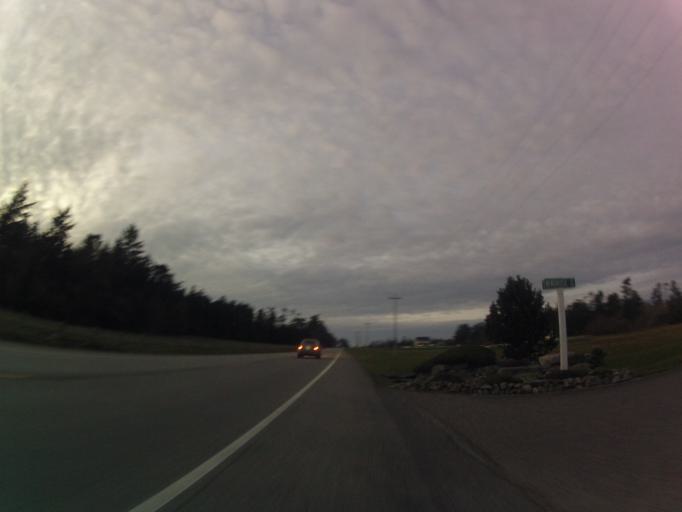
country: US
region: Washington
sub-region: Island County
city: Coupeville
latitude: 48.1728
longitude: -122.6807
